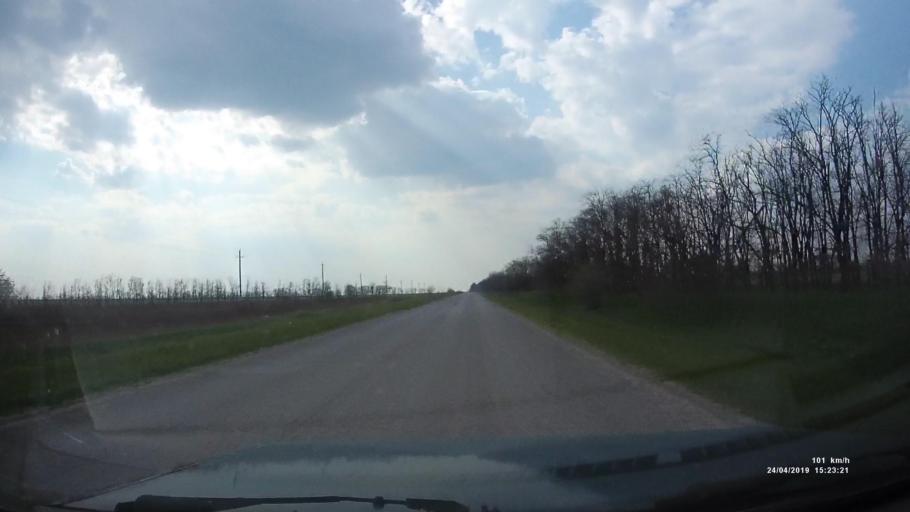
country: RU
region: Rostov
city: Remontnoye
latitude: 46.5429
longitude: 43.0917
